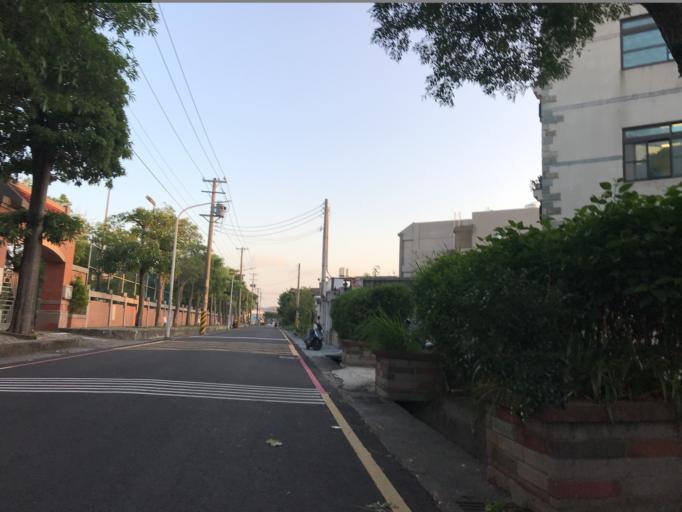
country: TW
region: Taiwan
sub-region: Hsinchu
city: Hsinchu
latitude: 24.8068
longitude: 120.9403
